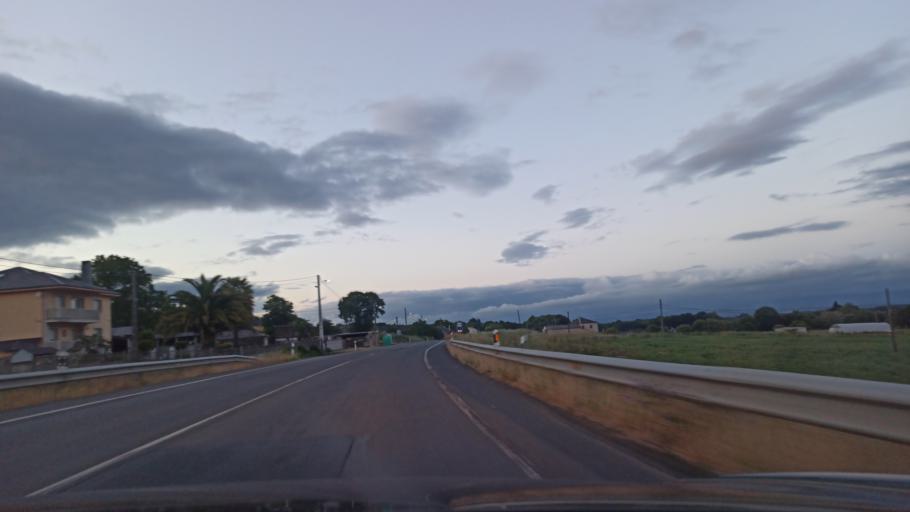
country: ES
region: Galicia
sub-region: Provincia de Lugo
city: Ourol
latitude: 42.9442
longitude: -7.6269
